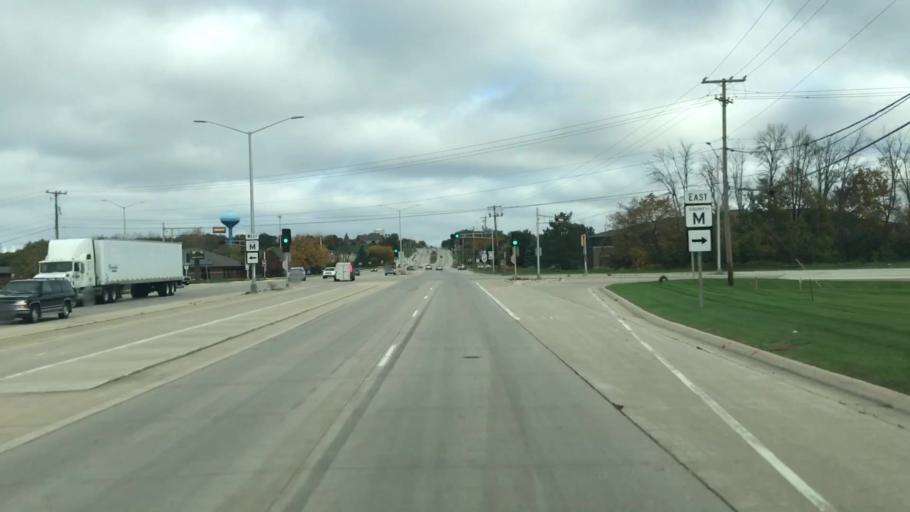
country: US
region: Wisconsin
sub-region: Waukesha County
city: Pewaukee
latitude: 43.0677
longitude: -88.2250
